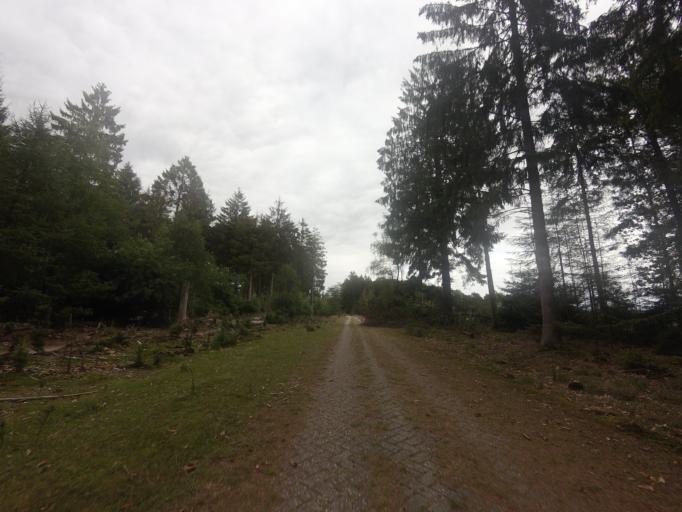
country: NL
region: Drenthe
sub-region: Gemeente Westerveld
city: Dwingeloo
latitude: 52.9157
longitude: 6.3086
